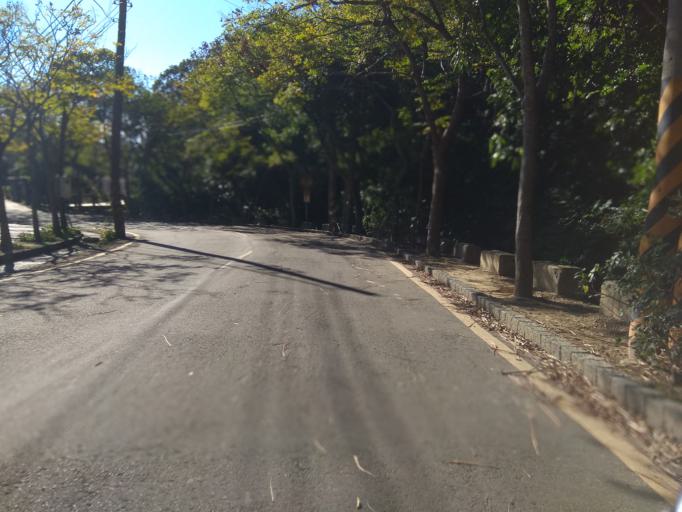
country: TW
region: Taiwan
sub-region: Hsinchu
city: Zhubei
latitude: 24.8609
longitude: 121.1040
